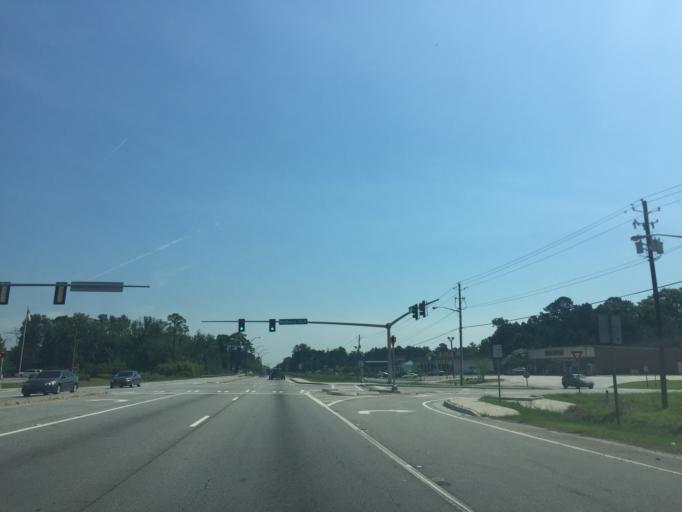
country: US
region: Georgia
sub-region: Bryan County
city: Richmond Hill
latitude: 31.9532
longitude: -81.3097
